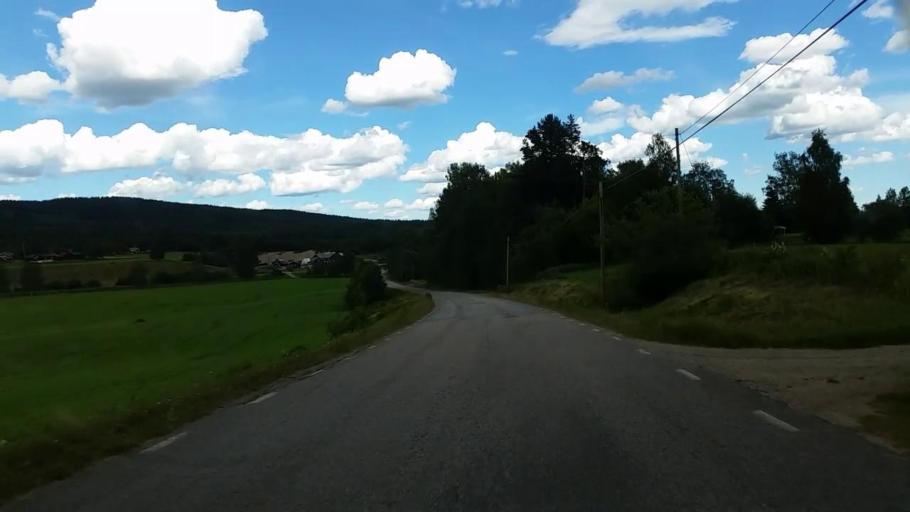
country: SE
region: Gaevleborg
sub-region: Ljusdals Kommun
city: Jaervsoe
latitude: 61.6680
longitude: 16.0913
